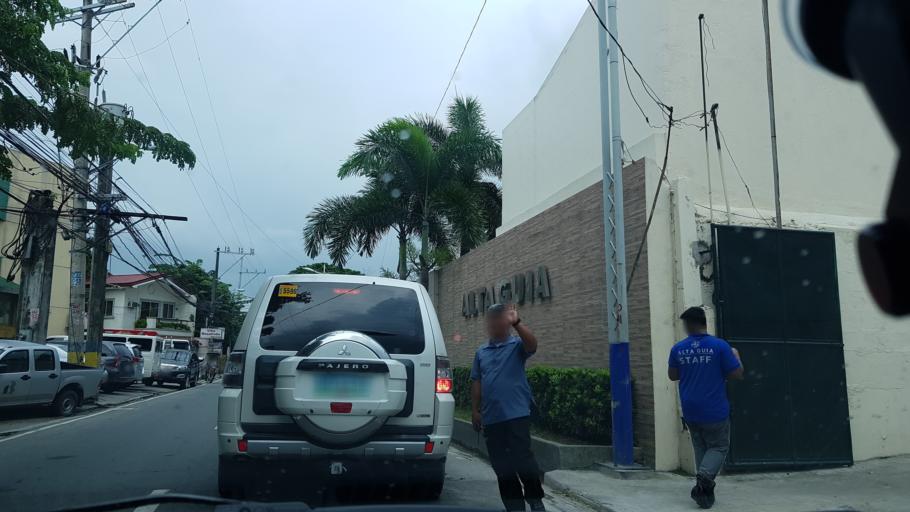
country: PH
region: Calabarzon
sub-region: Province of Rizal
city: Pateros
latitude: 14.5354
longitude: 121.0698
